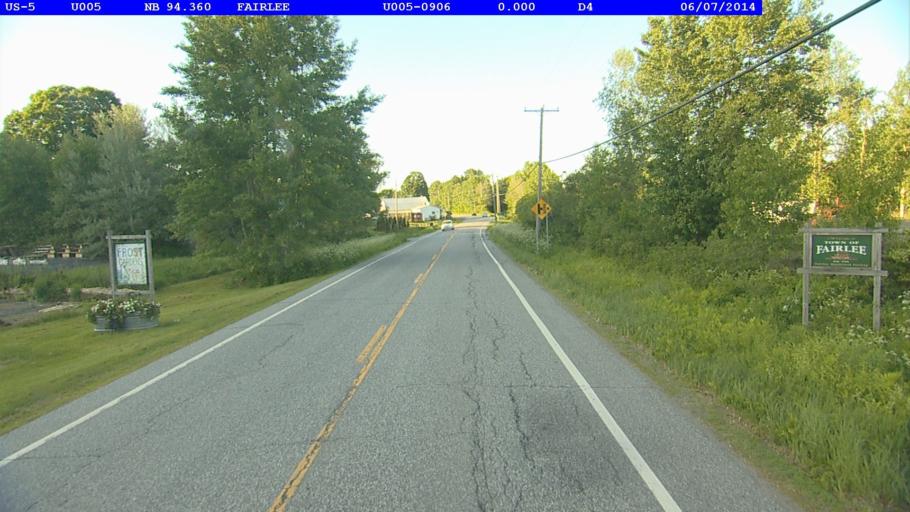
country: US
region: New Hampshire
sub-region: Grafton County
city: Orford
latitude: 43.8742
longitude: -72.1780
